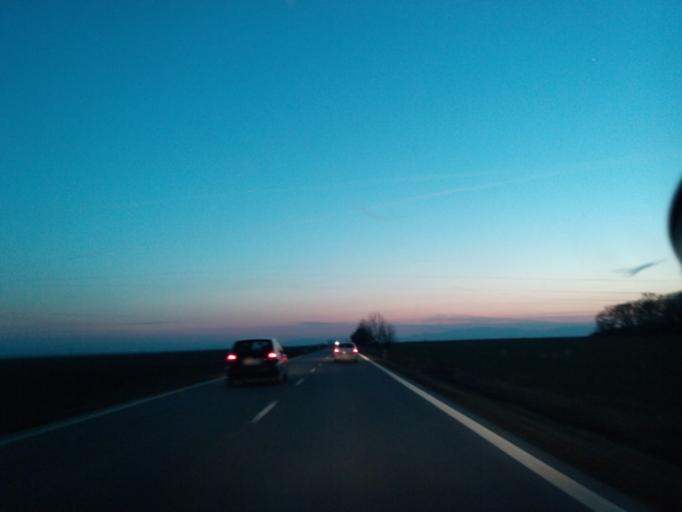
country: SK
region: Kosicky
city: Michalovce
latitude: 48.7071
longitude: 21.8252
